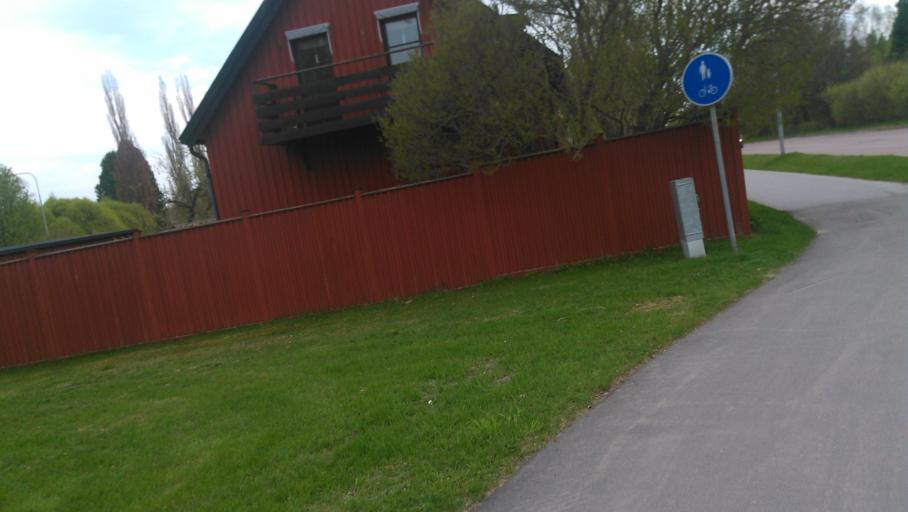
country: SE
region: Vaesterbotten
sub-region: Umea Kommun
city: Umea
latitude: 63.8105
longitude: 20.2693
